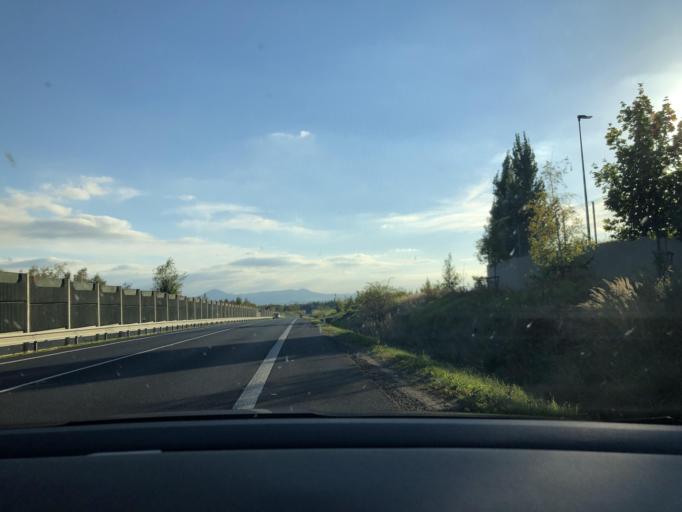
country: CZ
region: Ustecky
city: Libouchec
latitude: 50.7277
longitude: 14.0072
